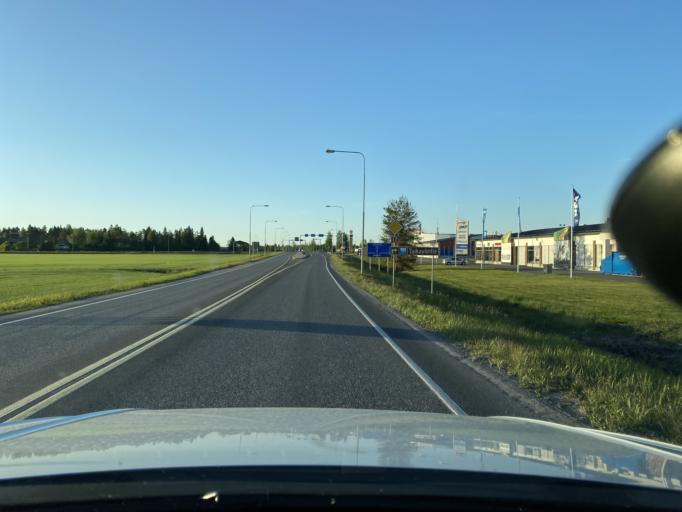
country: FI
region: Satakunta
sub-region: Pori
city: Huittinen
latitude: 61.1720
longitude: 22.6777
